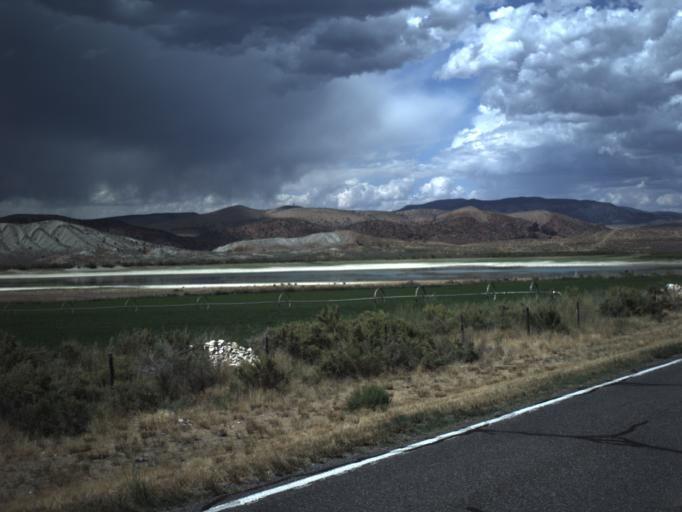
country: US
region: Utah
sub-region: Sanpete County
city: Gunnison
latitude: 39.1688
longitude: -111.7052
